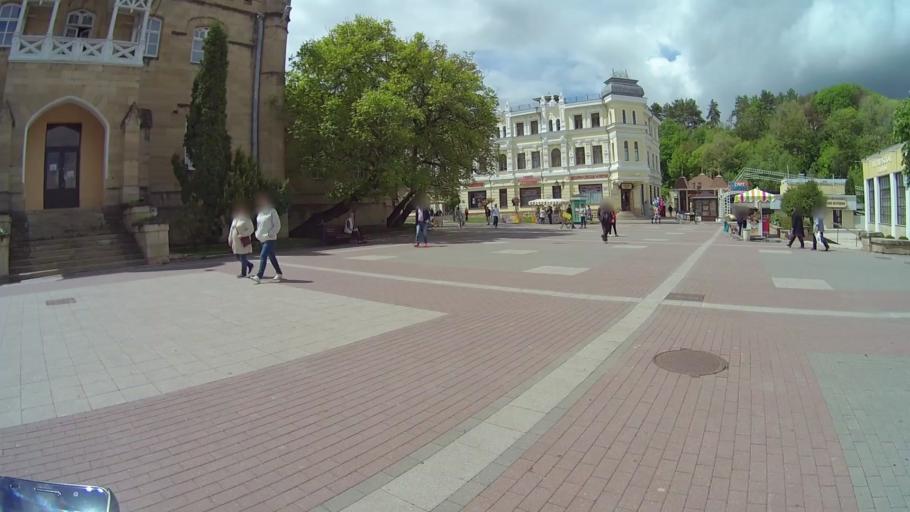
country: RU
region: Stavropol'skiy
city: Kislovodsk
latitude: 43.9008
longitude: 42.7168
